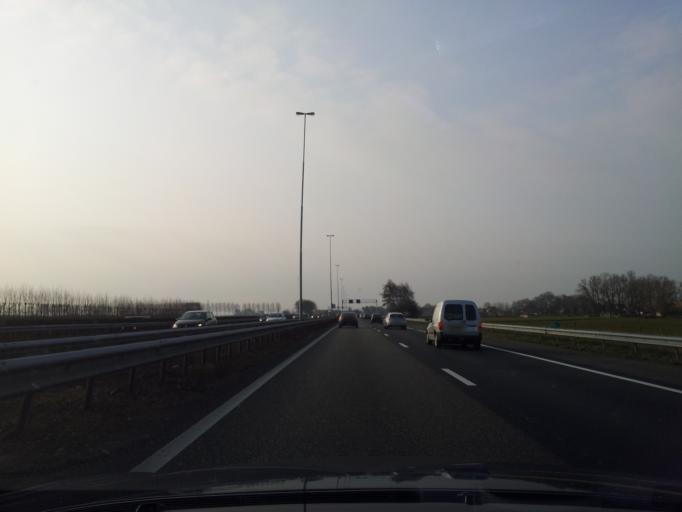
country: NL
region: North Brabant
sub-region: Gemeente Woudrichem
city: Almkerk
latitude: 51.7654
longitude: 4.9277
